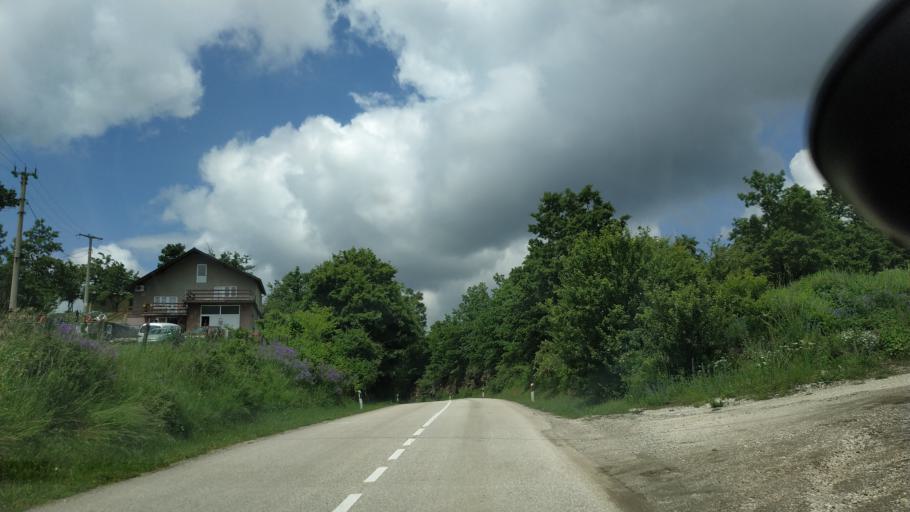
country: RS
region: Central Serbia
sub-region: Borski Okrug
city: Bor
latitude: 44.0853
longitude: 22.0070
